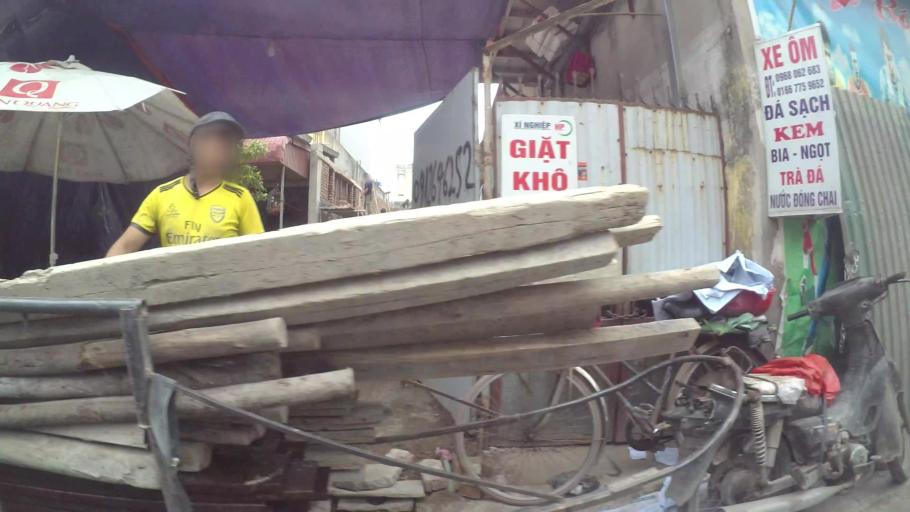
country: VN
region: Ha Noi
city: Hai BaTrung
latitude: 20.9898
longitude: 105.8886
